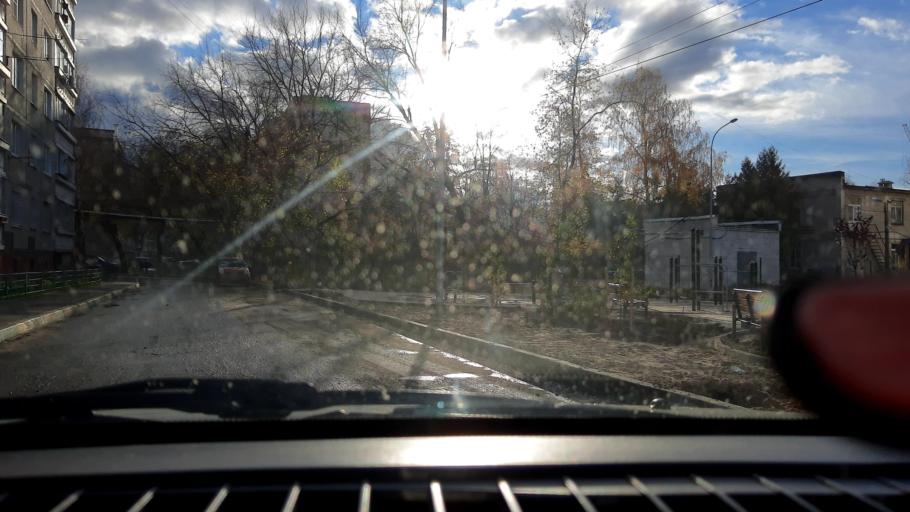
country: RU
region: Nizjnij Novgorod
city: Nizhniy Novgorod
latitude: 56.2774
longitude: 43.9479
